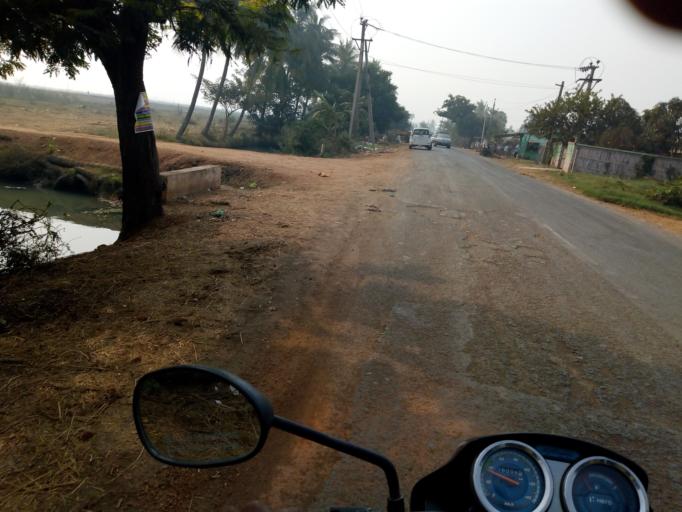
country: IN
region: Andhra Pradesh
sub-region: West Godavari
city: Tadepallegudem
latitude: 16.7444
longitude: 81.4196
